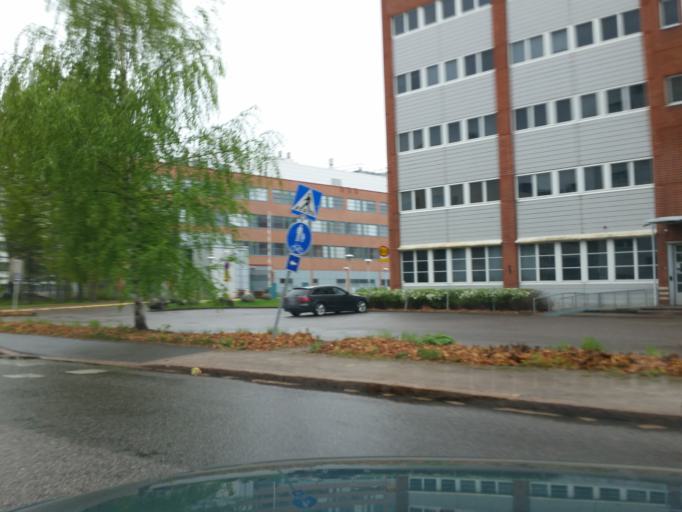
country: FI
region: Uusimaa
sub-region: Helsinki
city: Teekkarikylae
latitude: 60.2188
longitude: 24.8787
